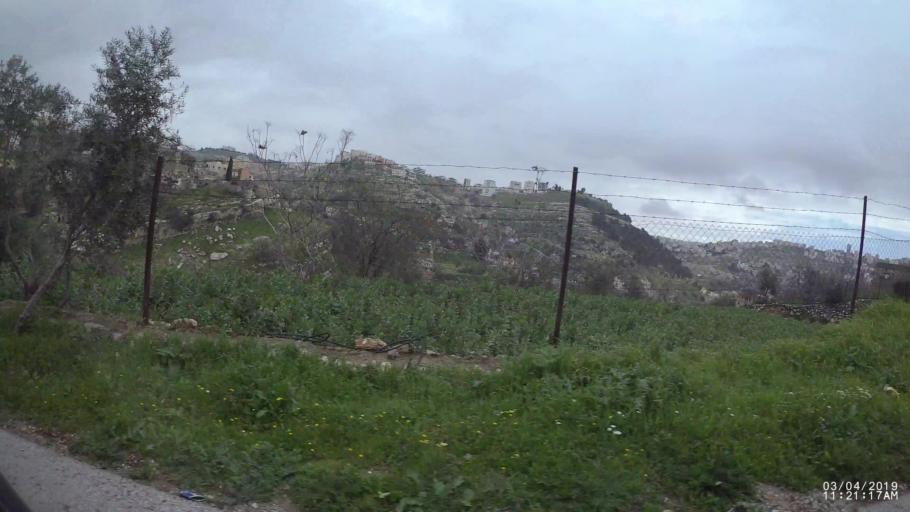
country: JO
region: Amman
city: Wadi as Sir
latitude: 31.9589
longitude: 35.8123
